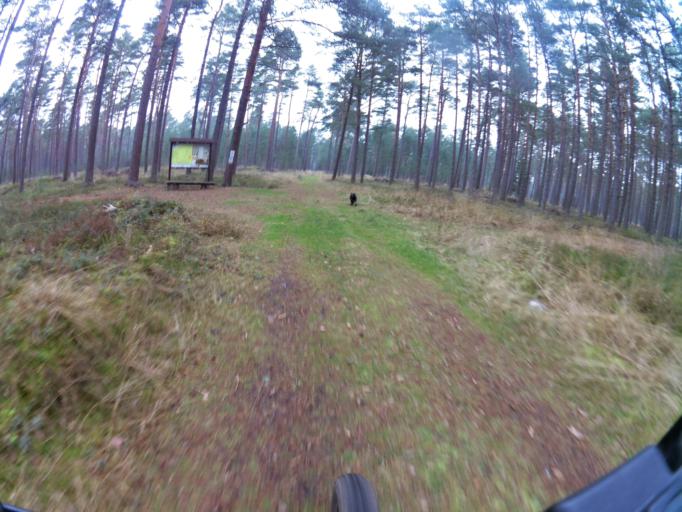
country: PL
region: West Pomeranian Voivodeship
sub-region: Powiat gryficki
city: Cerkwica
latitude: 54.1050
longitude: 15.1437
